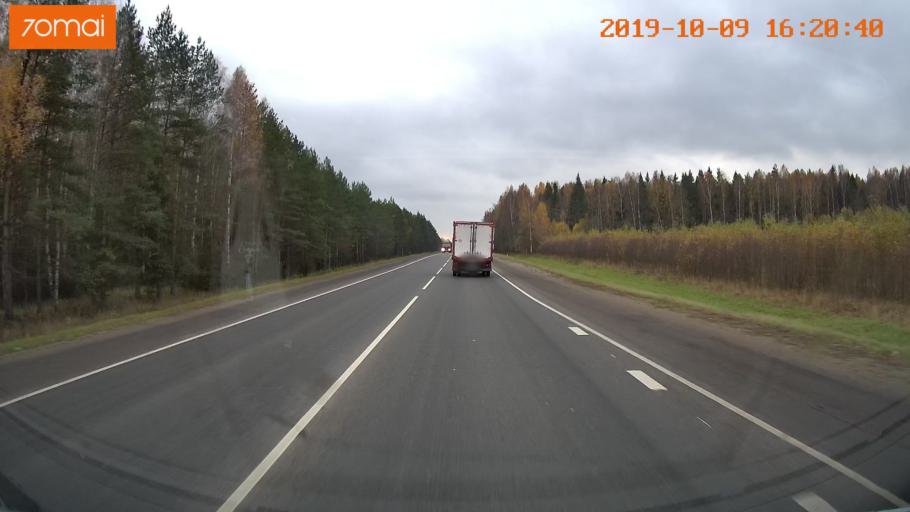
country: RU
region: Kostroma
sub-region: Kostromskoy Rayon
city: Kostroma
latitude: 57.7034
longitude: 40.8915
